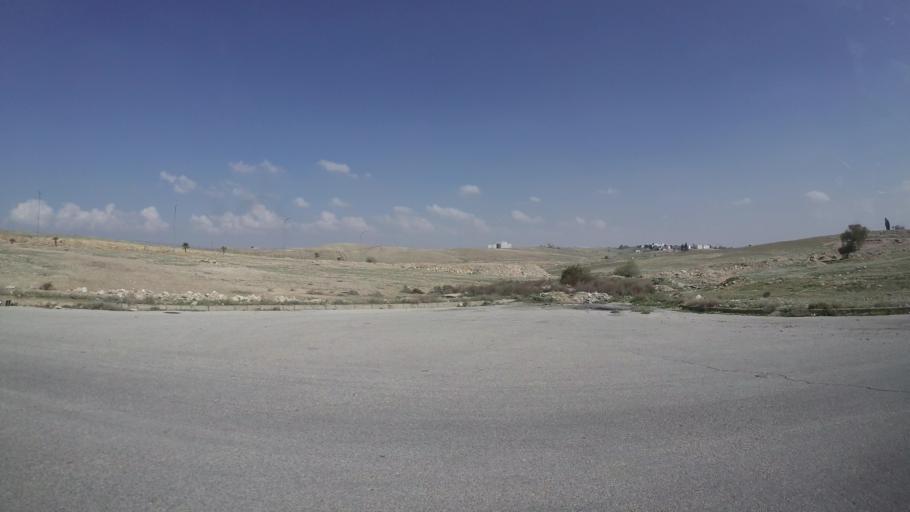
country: JO
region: Zarqa
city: Zarqa
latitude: 32.0738
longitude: 36.1136
